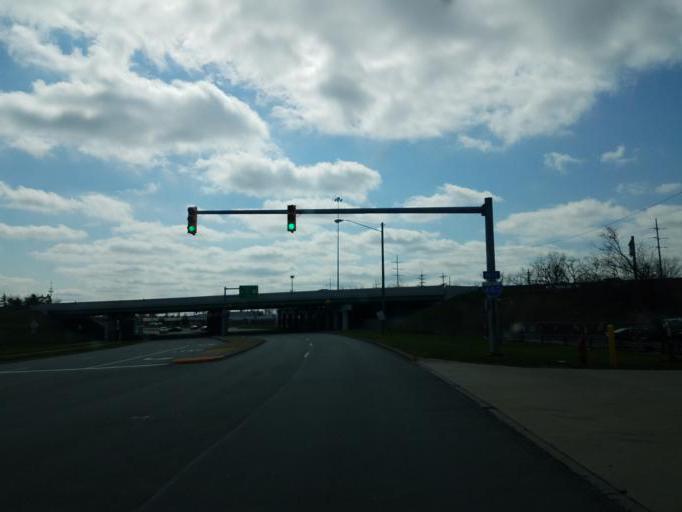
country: US
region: Ohio
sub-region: Cuyahoga County
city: Bedford Heights
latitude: 41.4255
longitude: -81.5227
